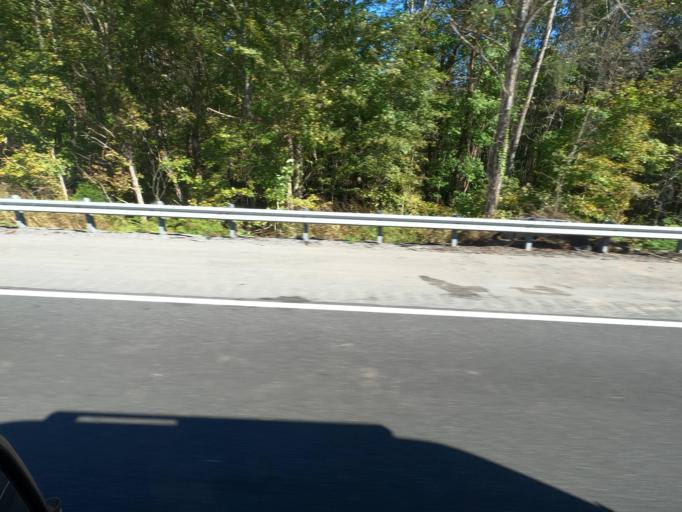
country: US
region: Tennessee
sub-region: Williamson County
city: Fairview
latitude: 36.0243
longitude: -87.1905
